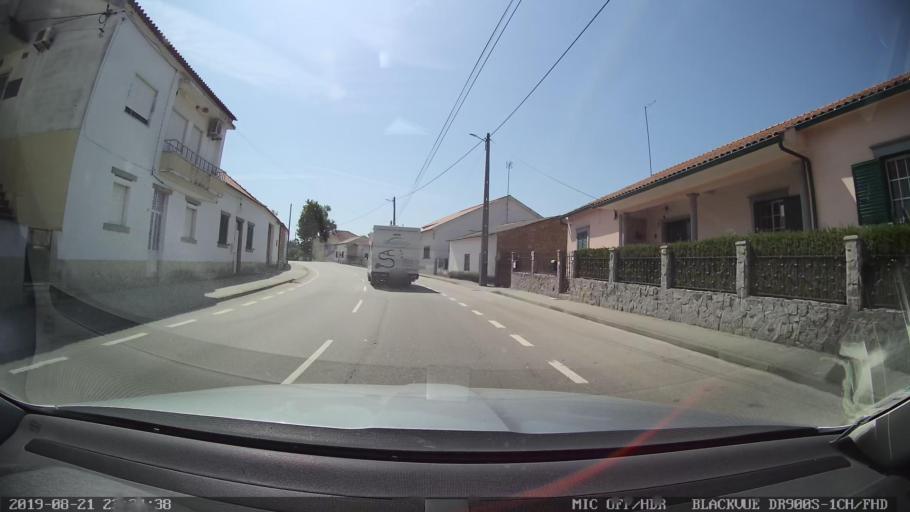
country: PT
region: Guarda
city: Alcains
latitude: 39.8801
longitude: -7.3961
